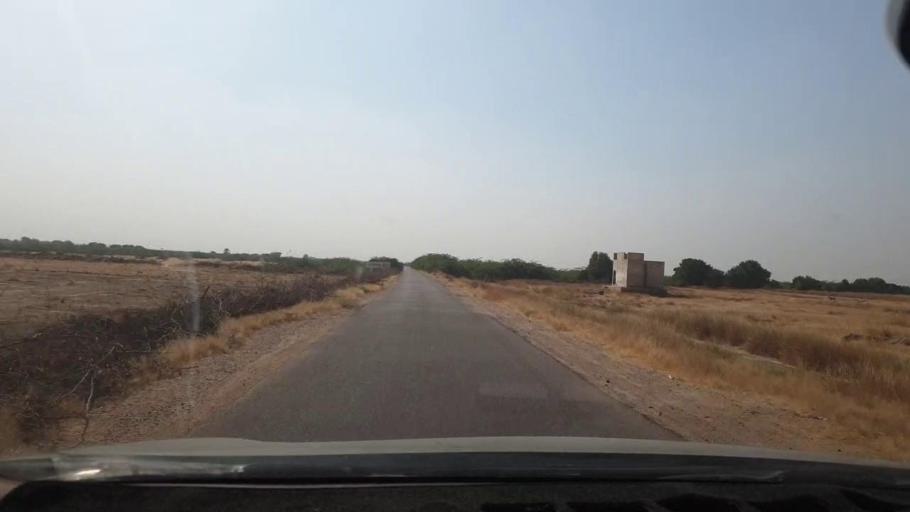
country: PK
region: Sindh
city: Malir Cantonment
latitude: 25.1064
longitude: 67.2003
